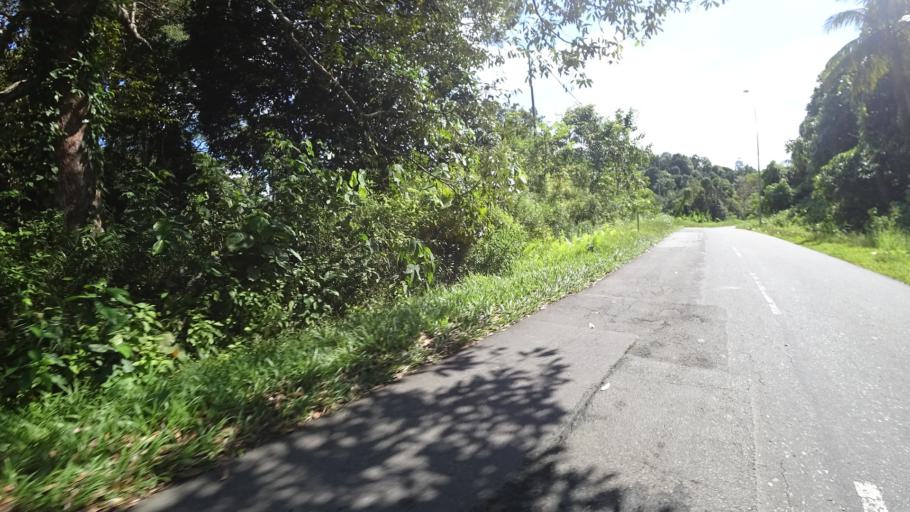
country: BN
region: Tutong
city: Tutong
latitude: 4.7558
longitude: 114.7909
